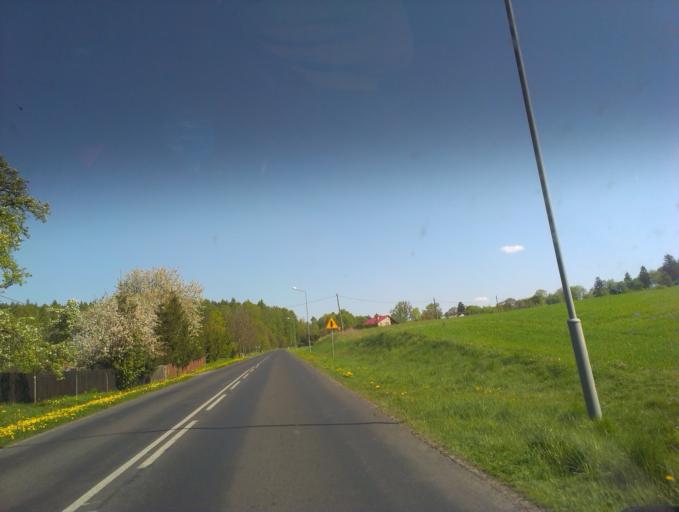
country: PL
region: West Pomeranian Voivodeship
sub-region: Powiat swidwinski
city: Polczyn-Zdroj
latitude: 53.7979
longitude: 16.0718
